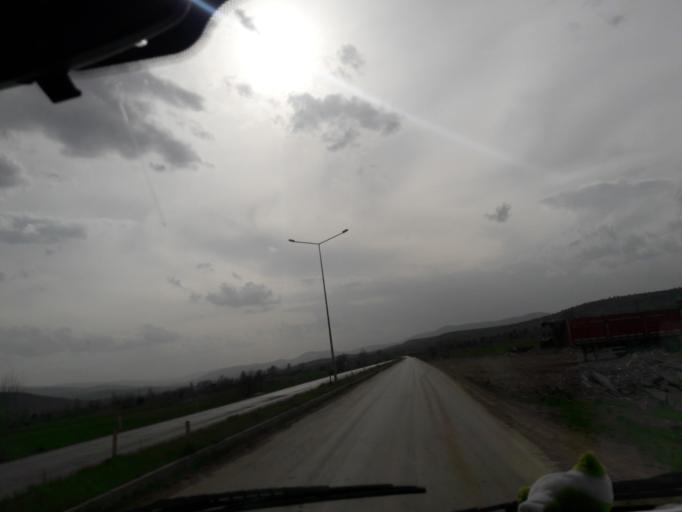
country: TR
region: Gumushane
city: Siran
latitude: 40.1772
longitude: 39.1051
